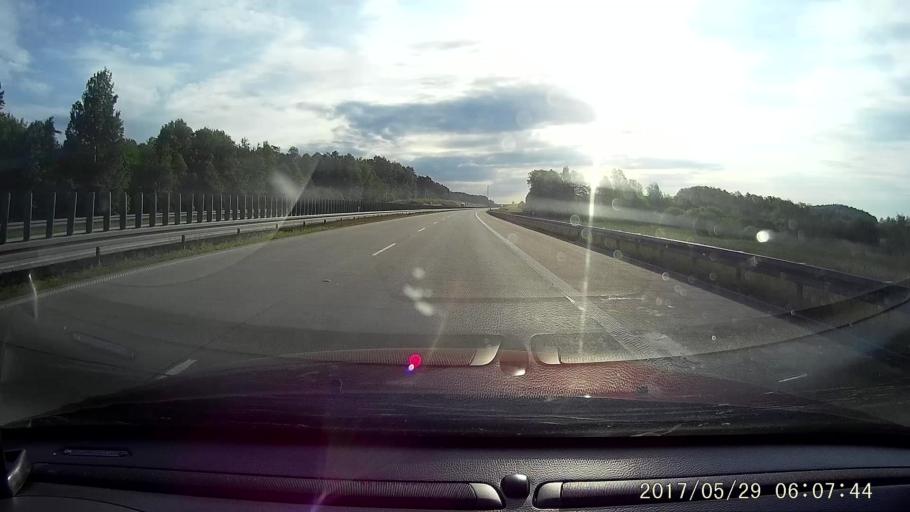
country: PL
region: Lower Silesian Voivodeship
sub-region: Powiat zgorzelecki
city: Lagow
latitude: 51.1980
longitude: 15.1283
